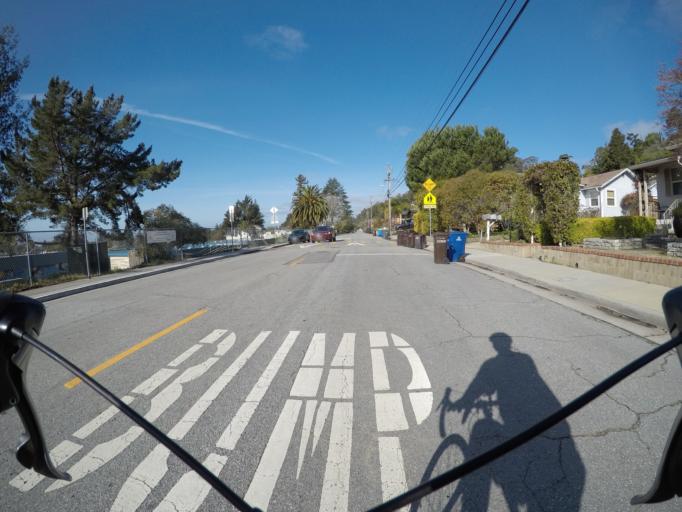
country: US
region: California
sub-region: Santa Cruz County
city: Live Oak
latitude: 36.9916
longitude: -121.9955
